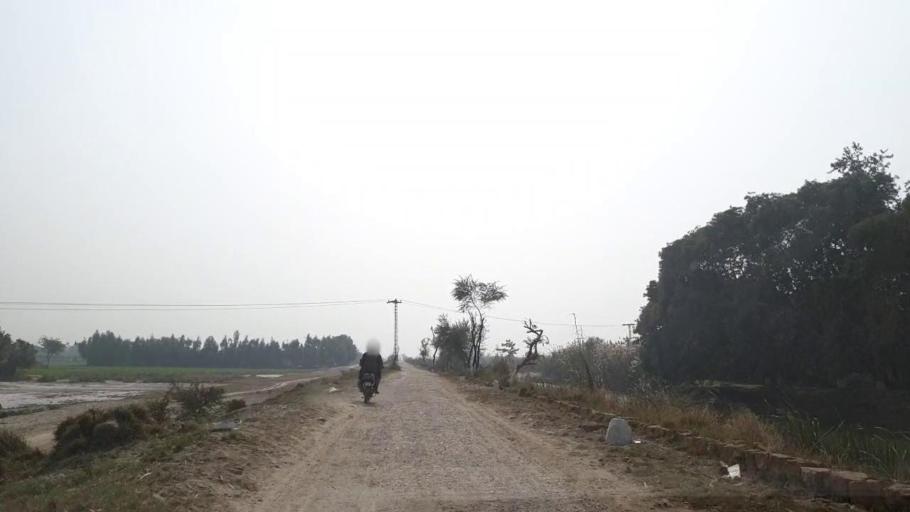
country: PK
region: Sindh
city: Matiari
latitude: 25.6430
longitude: 68.5606
